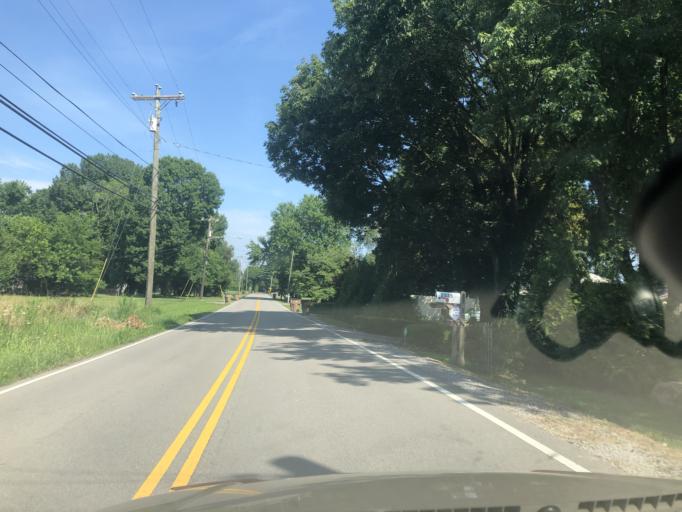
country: US
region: Tennessee
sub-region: Davidson County
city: Lakewood
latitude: 36.2343
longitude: -86.7001
